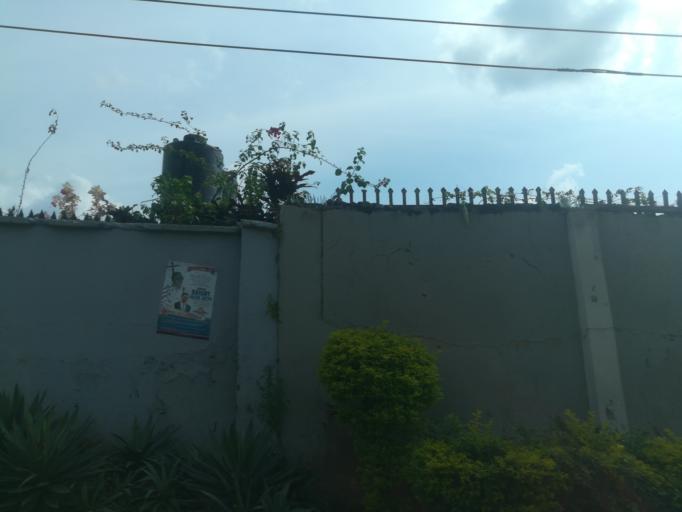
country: NG
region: Oyo
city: Ibadan
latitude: 7.3722
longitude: 3.8345
